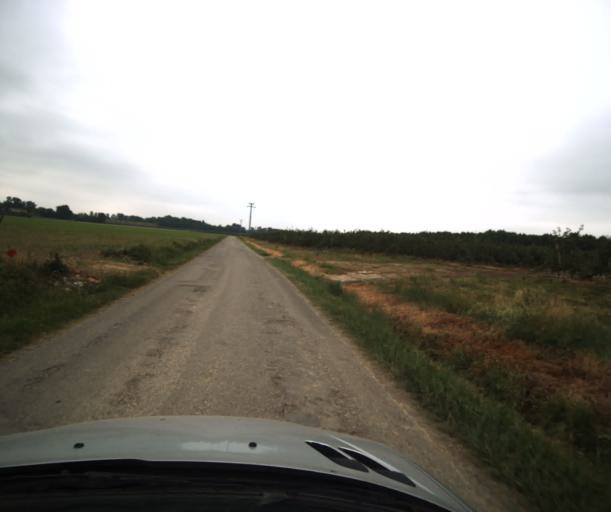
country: FR
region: Midi-Pyrenees
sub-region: Departement du Tarn-et-Garonne
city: Saint-Nicolas-de-la-Grave
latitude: 44.0702
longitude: 0.9878
